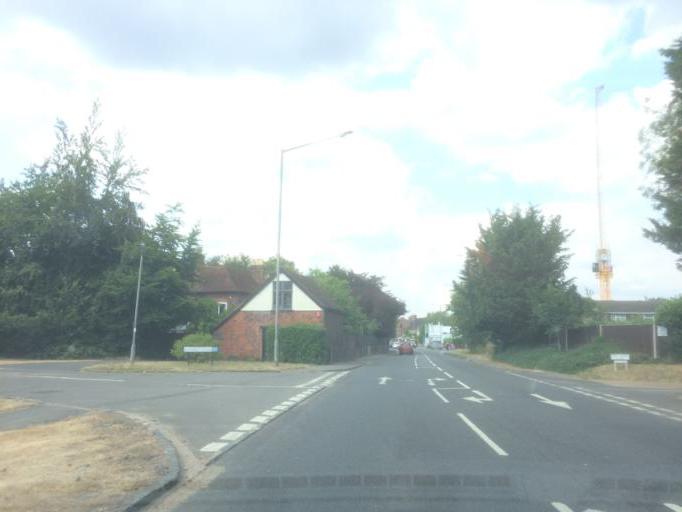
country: GB
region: England
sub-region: Buckinghamshire
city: Farnham Royal
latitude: 51.5521
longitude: -0.6156
